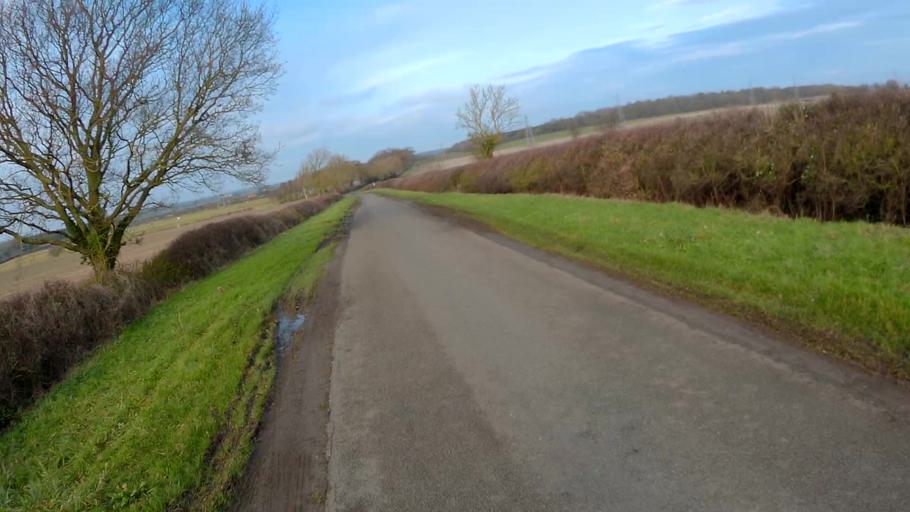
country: GB
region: England
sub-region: Lincolnshire
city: Bourne
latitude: 52.7567
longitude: -0.4185
